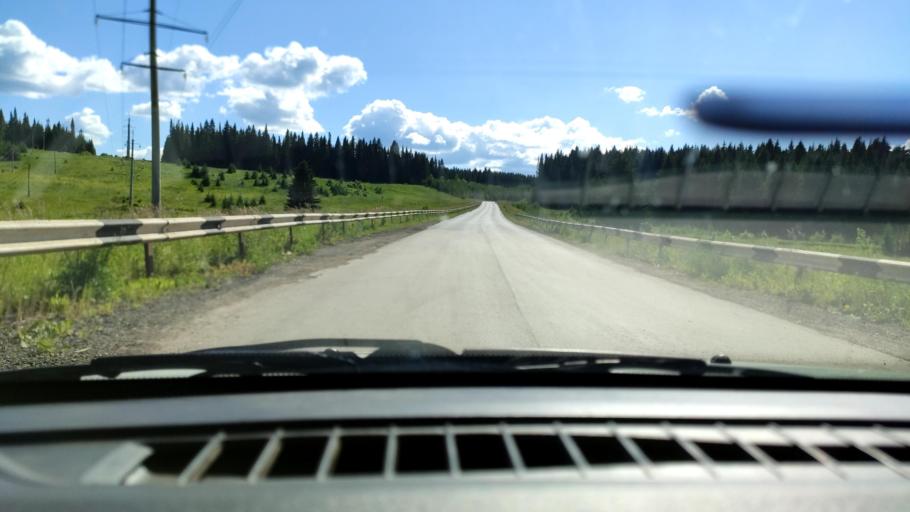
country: RU
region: Perm
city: Uinskoye
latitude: 57.1167
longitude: 56.5488
